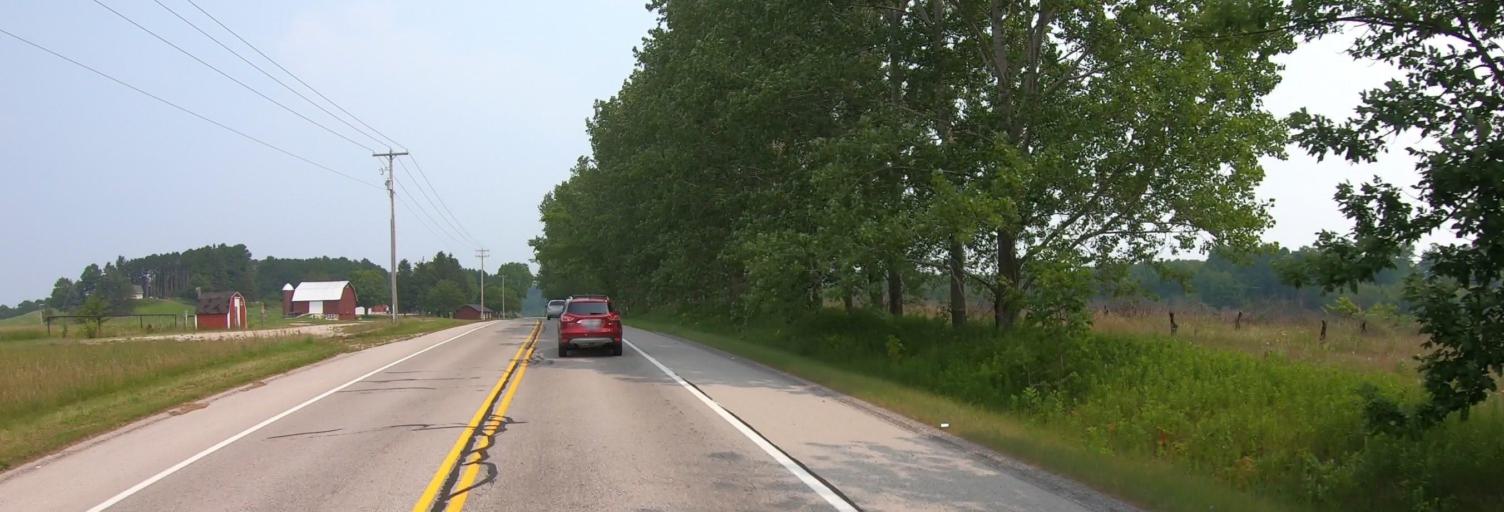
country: US
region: Michigan
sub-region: Leelanau County
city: Leland
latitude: 45.0889
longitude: -85.6669
